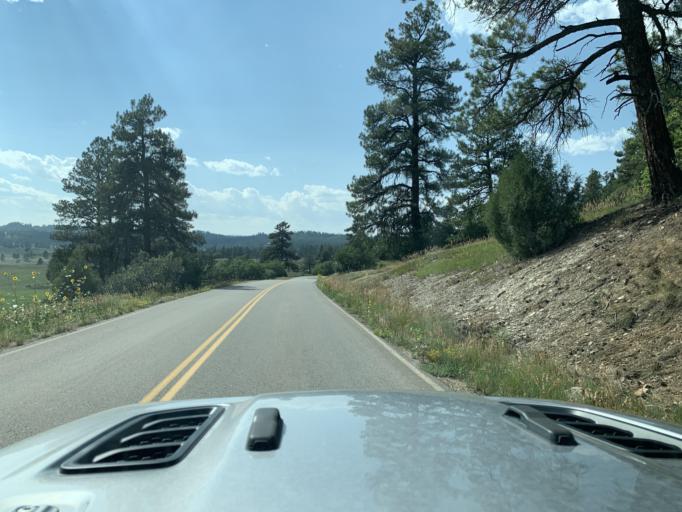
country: US
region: Colorado
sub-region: Archuleta County
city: Pagosa Springs
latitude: 37.2423
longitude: -107.0287
